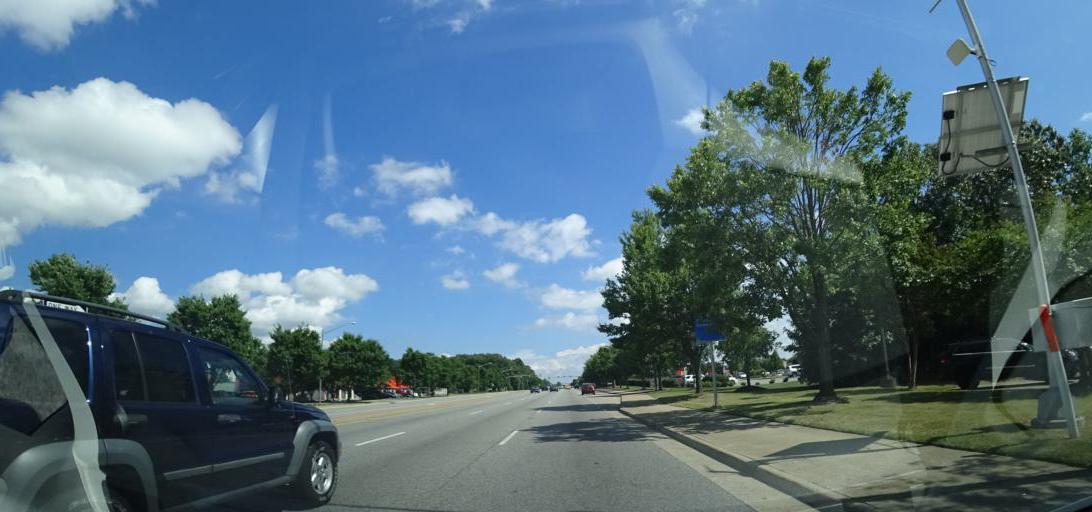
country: US
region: Virginia
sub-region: York County
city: Yorktown
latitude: 37.1328
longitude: -76.5157
